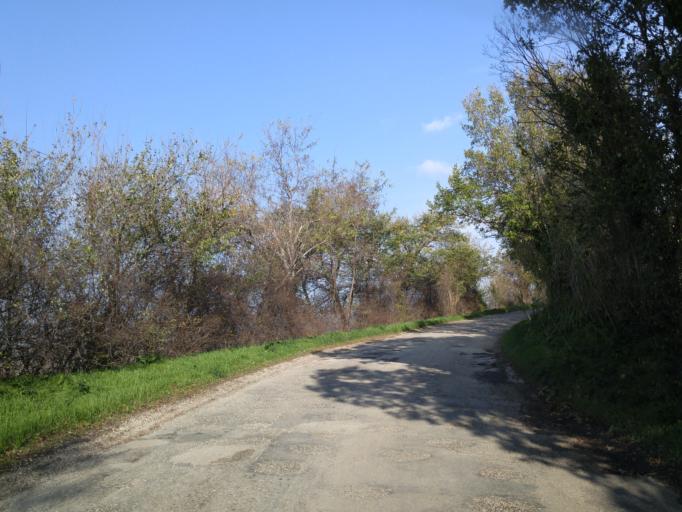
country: IT
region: The Marches
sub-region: Provincia di Pesaro e Urbino
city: Lucrezia
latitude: 43.8143
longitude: 12.9099
